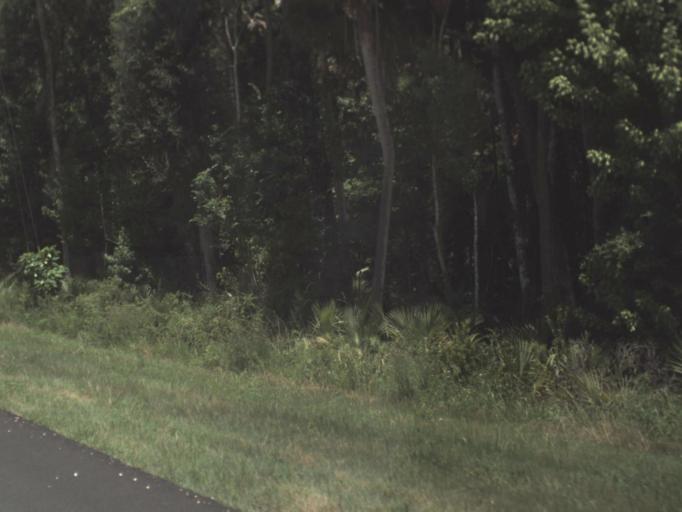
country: US
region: Florida
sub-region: Leon County
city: Woodville
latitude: 30.1443
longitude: -83.9686
